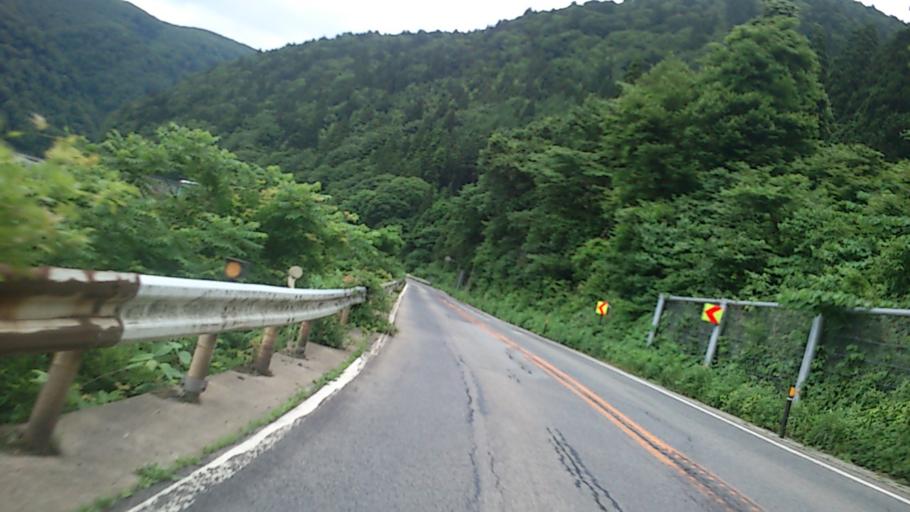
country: JP
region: Yamagata
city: Shinjo
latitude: 38.7492
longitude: 140.0818
